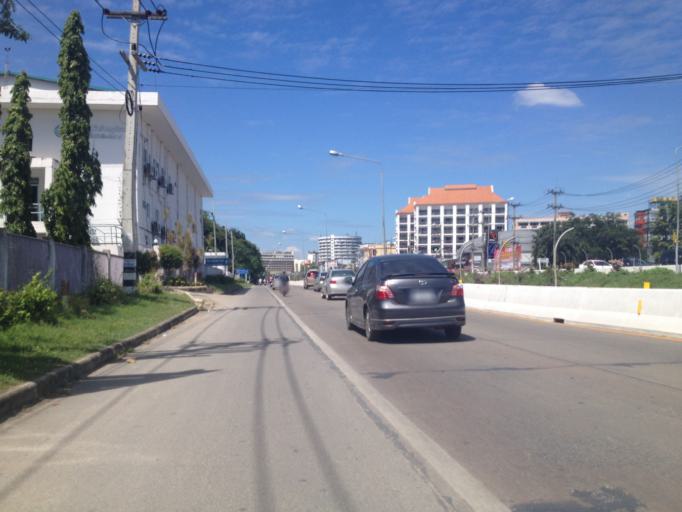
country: TH
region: Chiang Mai
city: Chiang Mai
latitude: 18.7966
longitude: 98.9614
